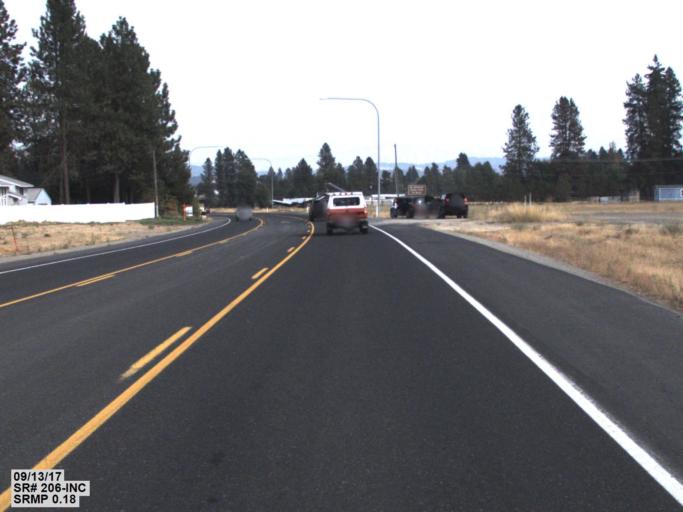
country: US
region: Washington
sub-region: Spokane County
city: Mead
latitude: 47.7871
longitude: -117.3495
